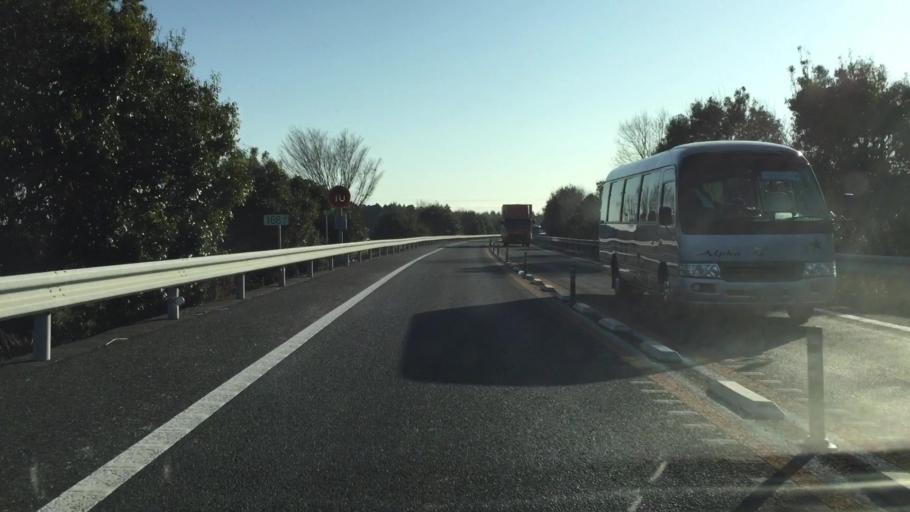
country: JP
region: Ibaraki
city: Ami
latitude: 35.9952
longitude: 140.2097
